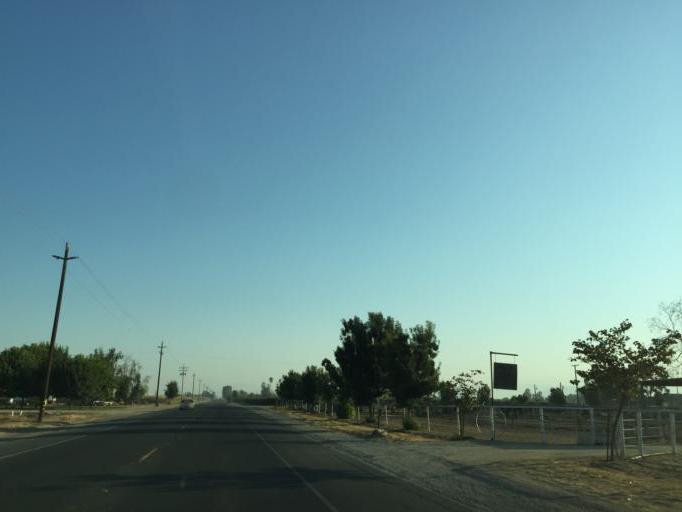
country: US
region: California
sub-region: Tulare County
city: Cutler
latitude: 36.4347
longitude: -119.2957
